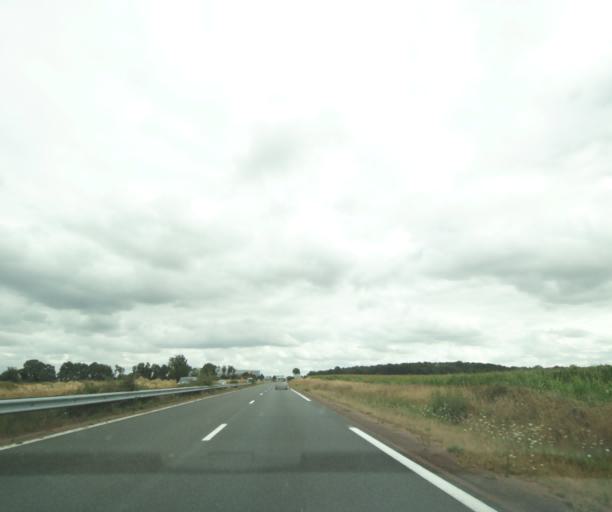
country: FR
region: Pays de la Loire
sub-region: Departement de la Vendee
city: Saint-Andre-Treize-Voies
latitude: 46.9042
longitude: -1.3858
